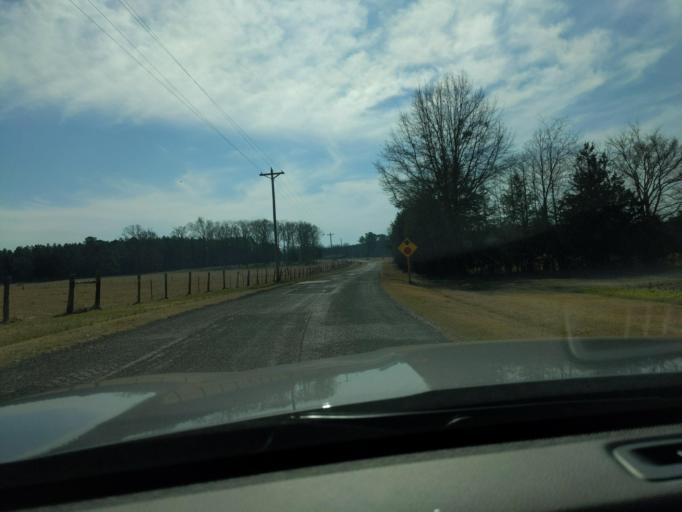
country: US
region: South Carolina
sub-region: Abbeville County
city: Calhoun Falls
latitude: 34.0870
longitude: -82.5434
